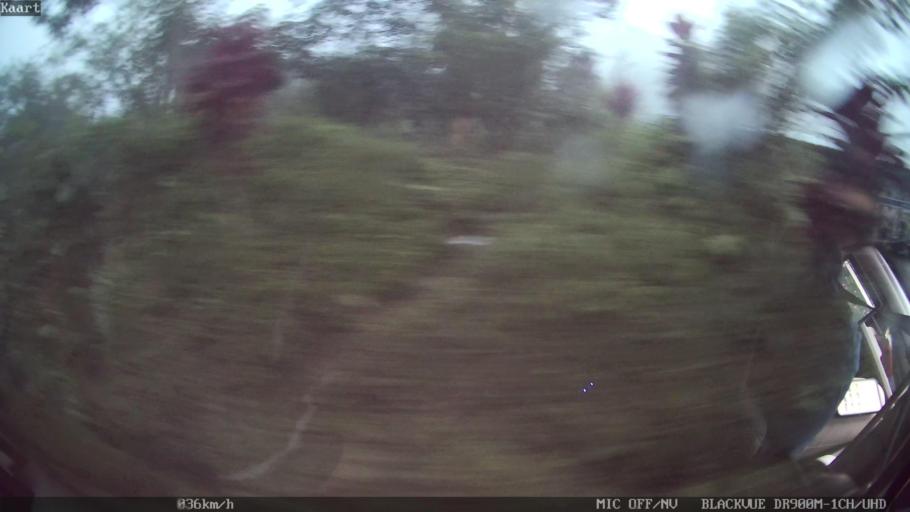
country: ID
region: Bali
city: Banjar Taro Kelod
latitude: -8.3326
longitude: 115.2867
